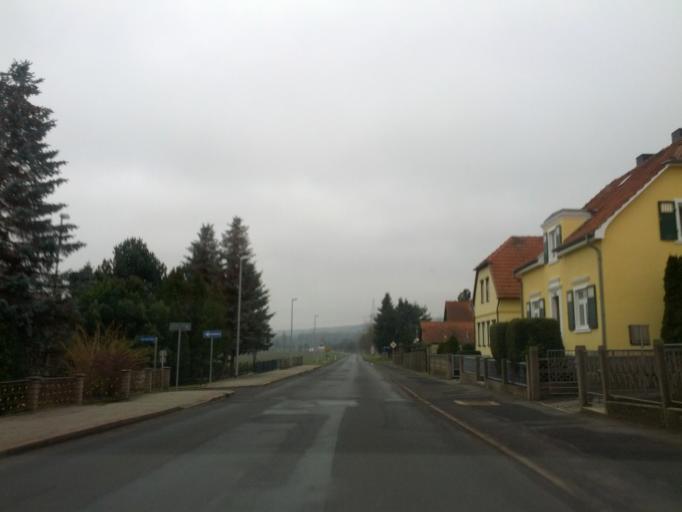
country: DE
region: Thuringia
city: Goldbach
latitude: 50.9898
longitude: 10.6586
